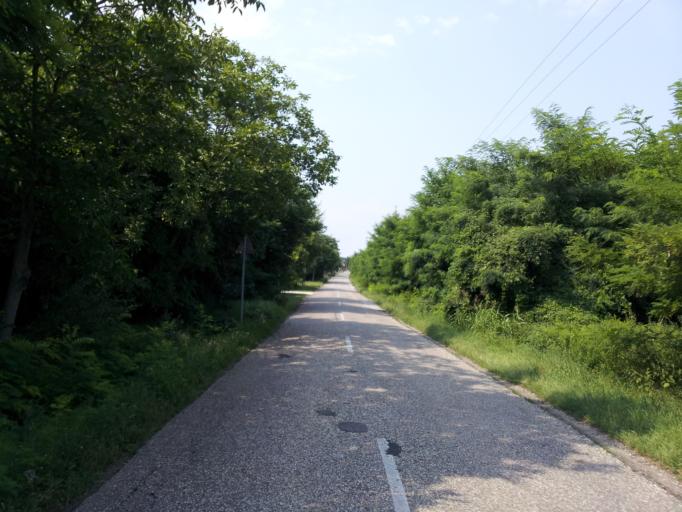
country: HU
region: Pest
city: Szigetujfalu
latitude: 47.2213
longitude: 18.9210
